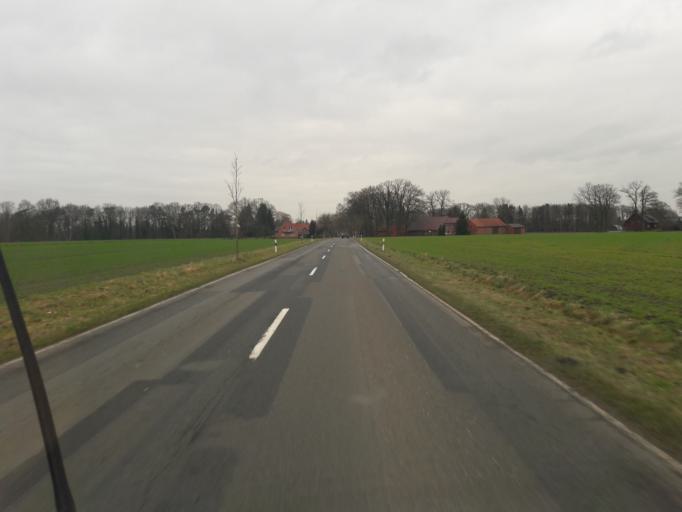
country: DE
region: Lower Saxony
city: Warmsen
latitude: 52.3961
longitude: 8.8579
